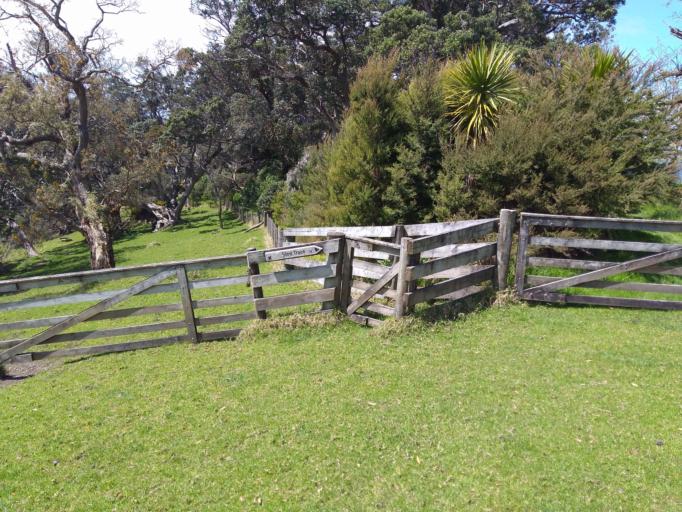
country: NZ
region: Auckland
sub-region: Auckland
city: Warkworth
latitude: -36.4443
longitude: 174.7716
